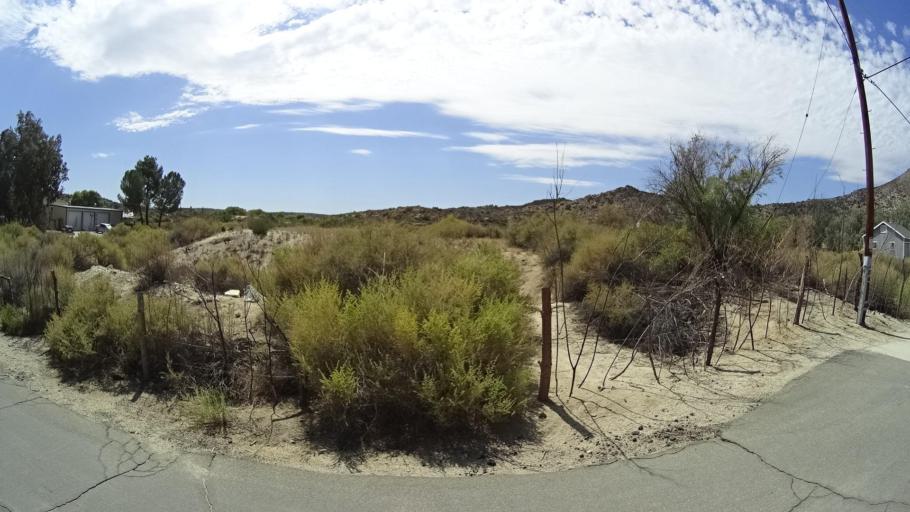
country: MX
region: Baja California
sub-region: Tecate
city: Cereso del Hongo
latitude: 32.6201
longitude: -116.1916
